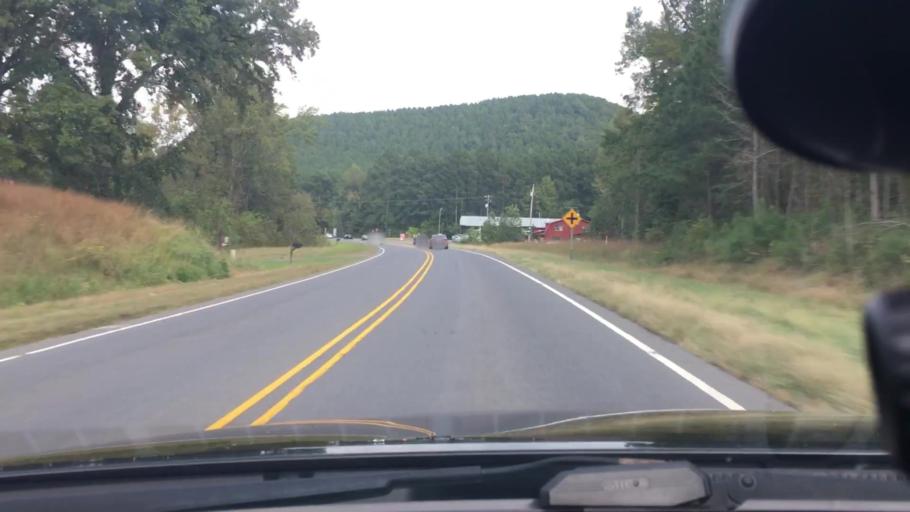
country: US
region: North Carolina
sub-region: Stanly County
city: Norwood
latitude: 35.3070
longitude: -80.0619
